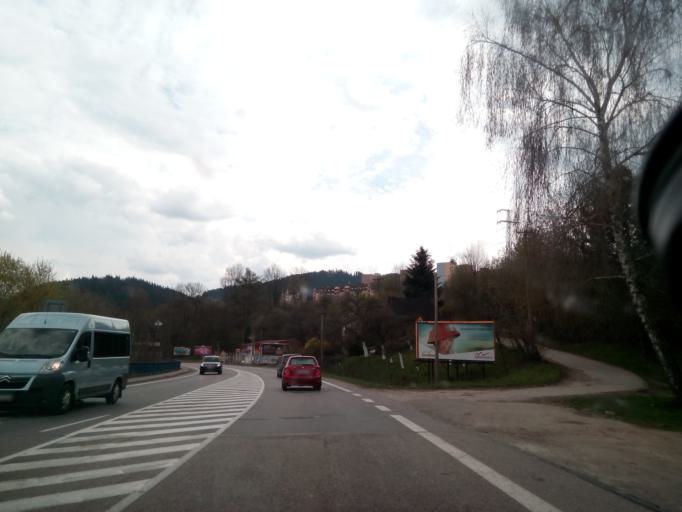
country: SK
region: Zilinsky
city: Ruzomberok
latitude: 49.0870
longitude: 19.2707
